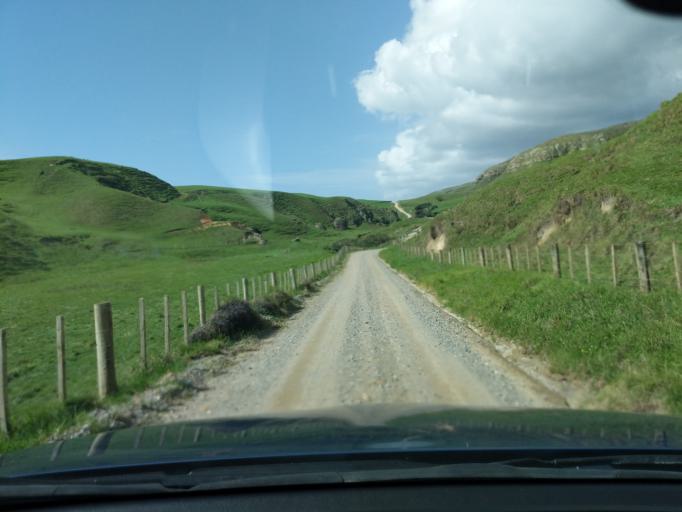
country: NZ
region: Tasman
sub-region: Tasman District
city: Takaka
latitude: -40.6533
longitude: 172.4187
